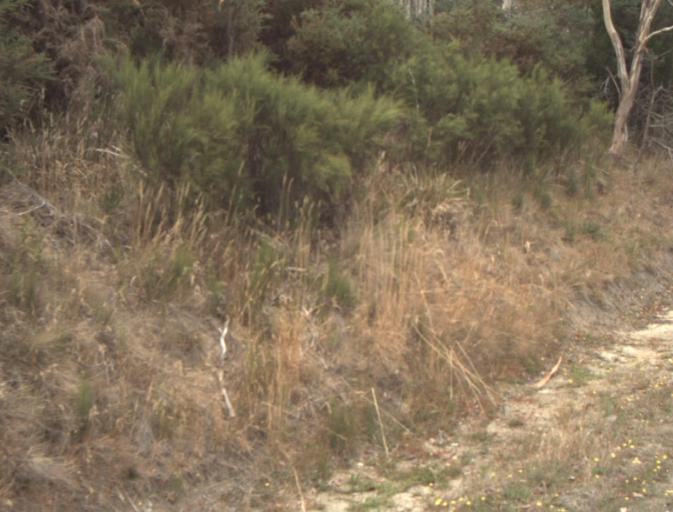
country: AU
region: Tasmania
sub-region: Northern Midlands
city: Evandale
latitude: -41.4954
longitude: 147.4217
